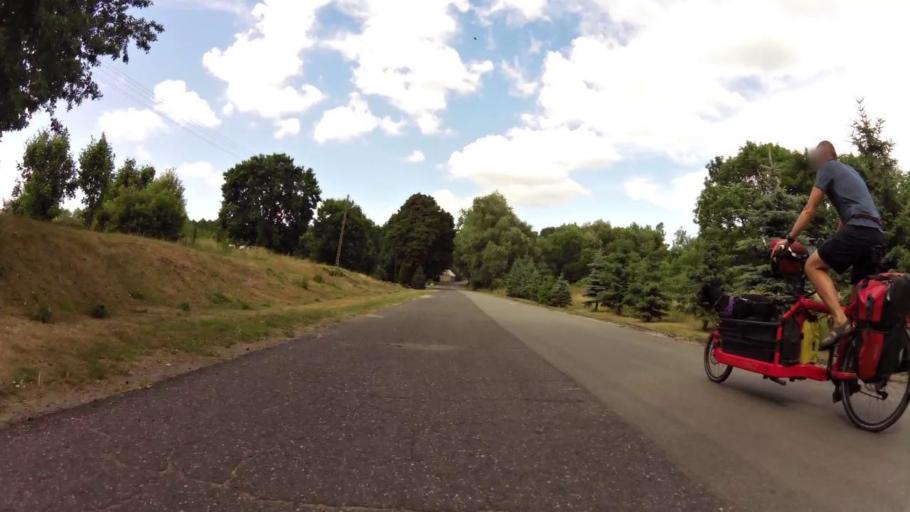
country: PL
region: West Pomeranian Voivodeship
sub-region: Powiat lobeski
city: Lobez
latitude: 53.6227
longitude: 15.6784
